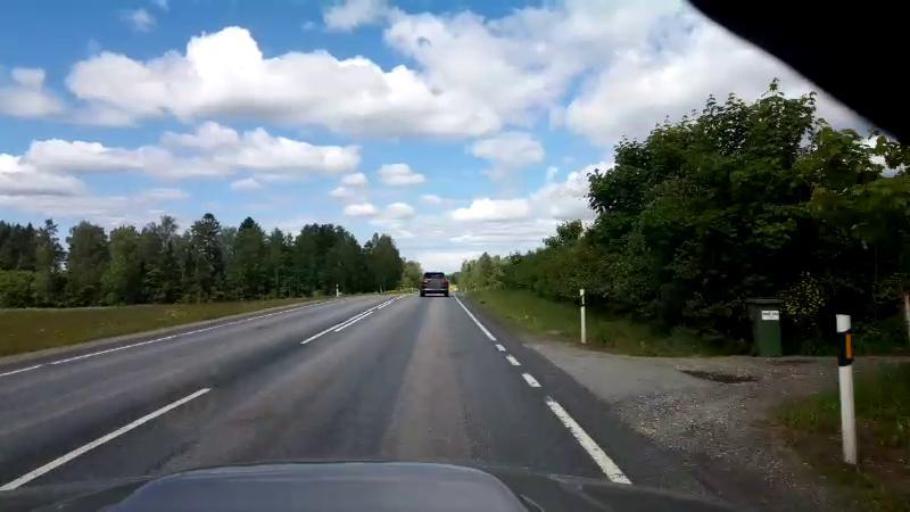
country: EE
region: Harju
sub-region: Saue linn
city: Saue
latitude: 59.1491
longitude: 24.5055
